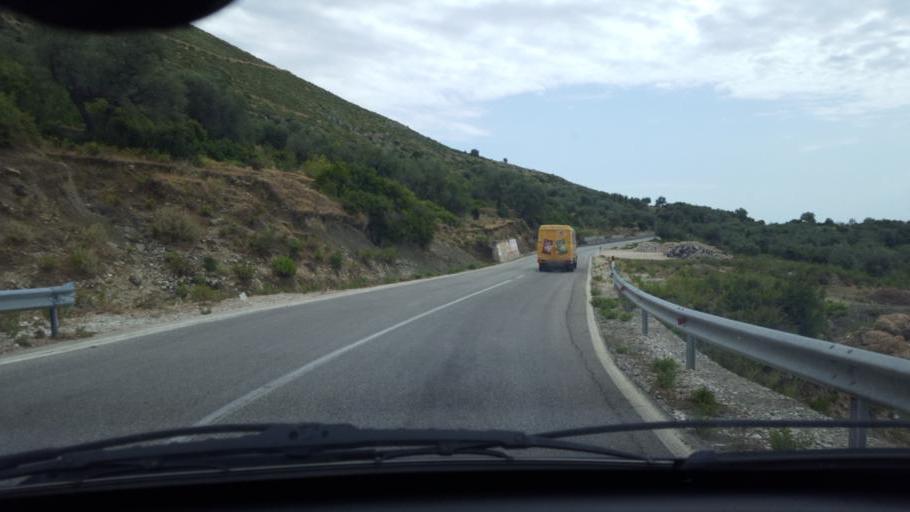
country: AL
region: Vlore
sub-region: Rrethi i Sarandes
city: Lukove
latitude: 40.0318
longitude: 19.8878
